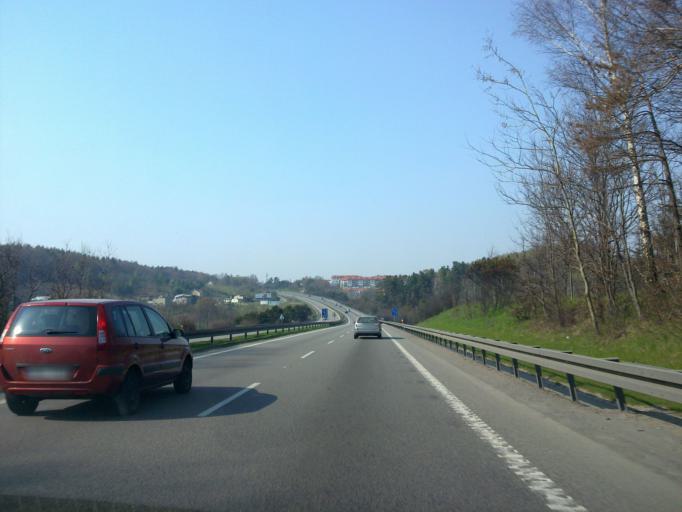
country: PL
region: Pomeranian Voivodeship
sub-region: Gdynia
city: Wielki Kack
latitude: 54.4585
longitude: 18.4890
